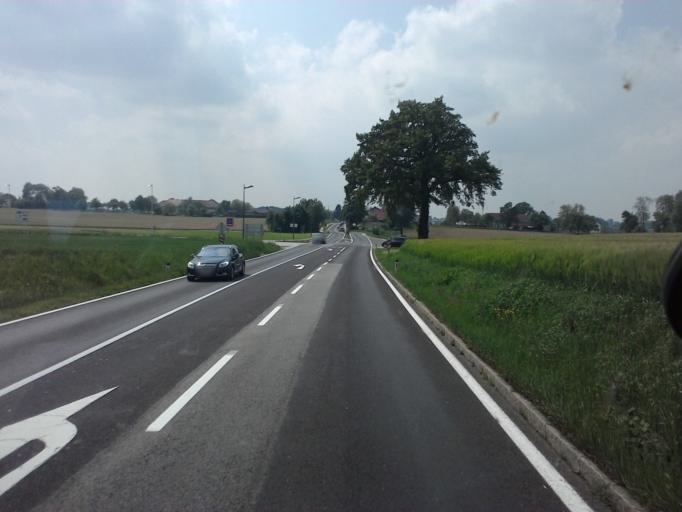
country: AT
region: Upper Austria
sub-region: Wels-Land
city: Sattledt
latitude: 48.0721
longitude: 14.0705
